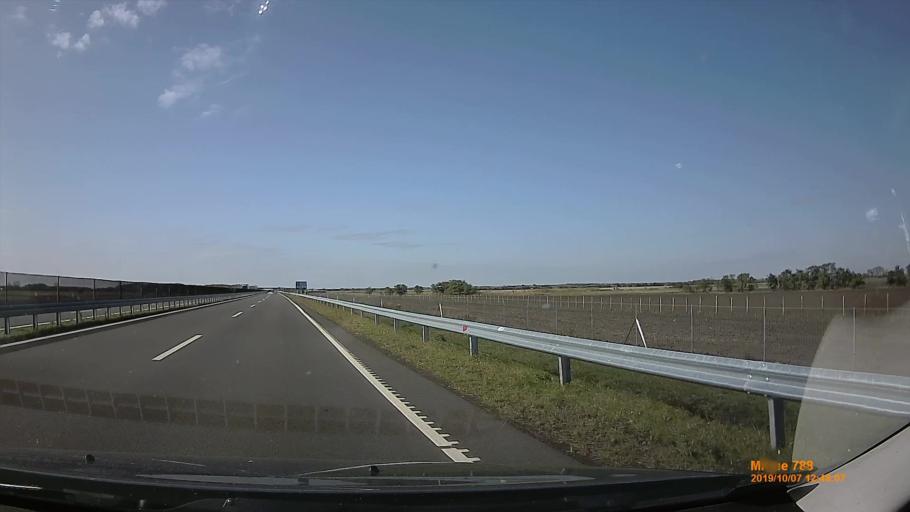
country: HU
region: Jasz-Nagykun-Szolnok
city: Cserkeszolo
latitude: 46.8827
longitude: 20.2290
